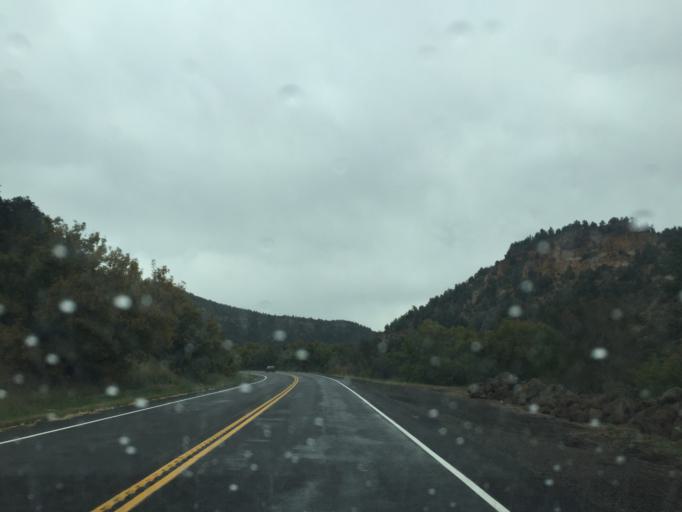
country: US
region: Utah
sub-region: Kane County
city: Kanab
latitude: 37.3526
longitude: -112.5978
